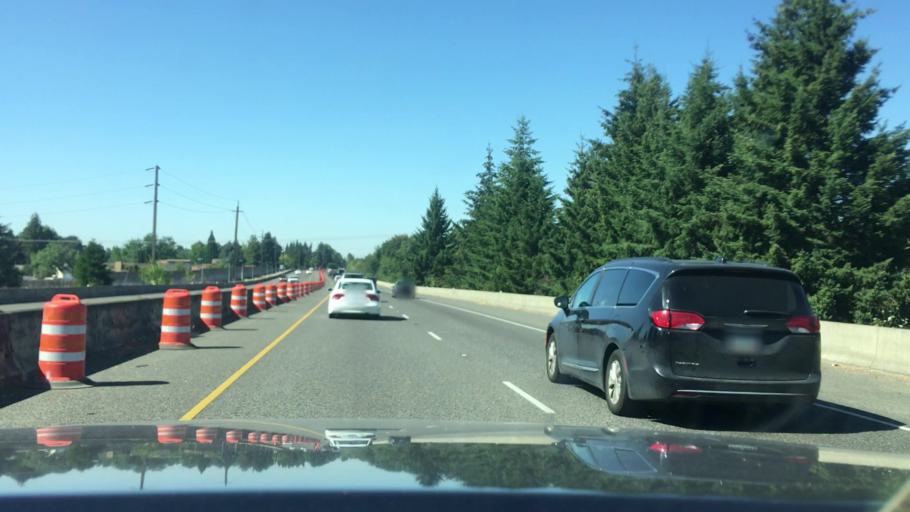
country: US
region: Oregon
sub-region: Lane County
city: Eugene
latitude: 44.0722
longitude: -123.1736
